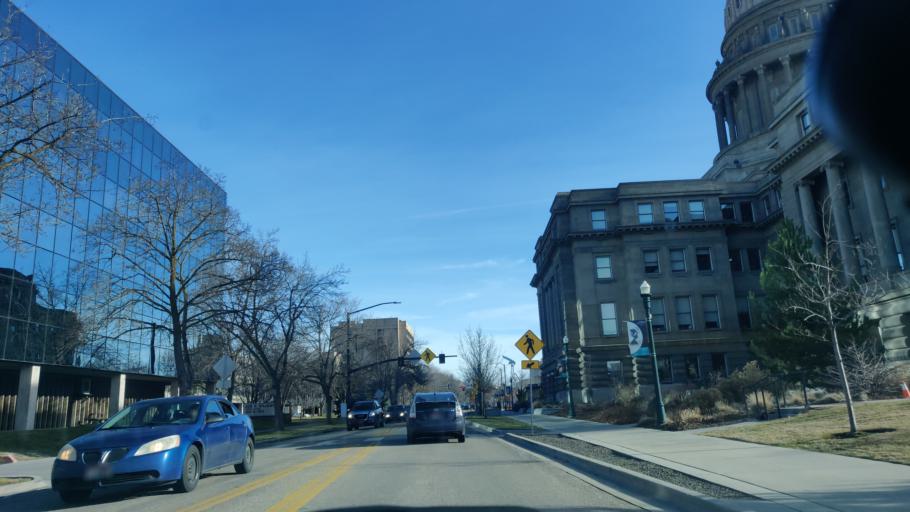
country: US
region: Idaho
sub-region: Ada County
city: Boise
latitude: 43.6185
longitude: -116.2002
